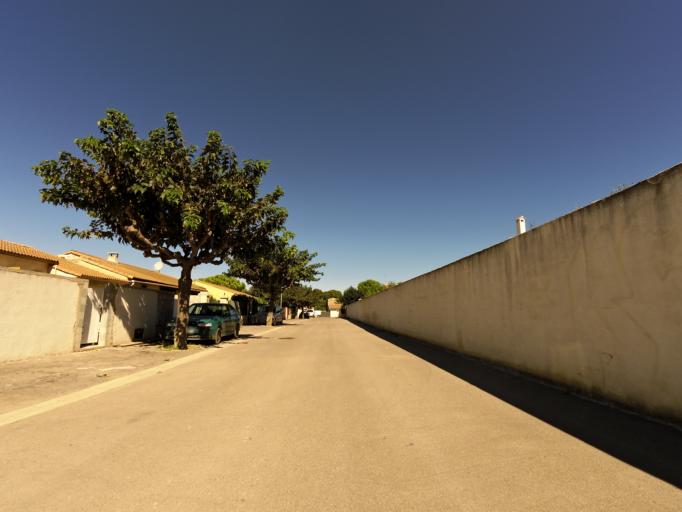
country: FR
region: Languedoc-Roussillon
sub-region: Departement du Gard
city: Codognan
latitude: 43.7283
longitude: 4.2196
